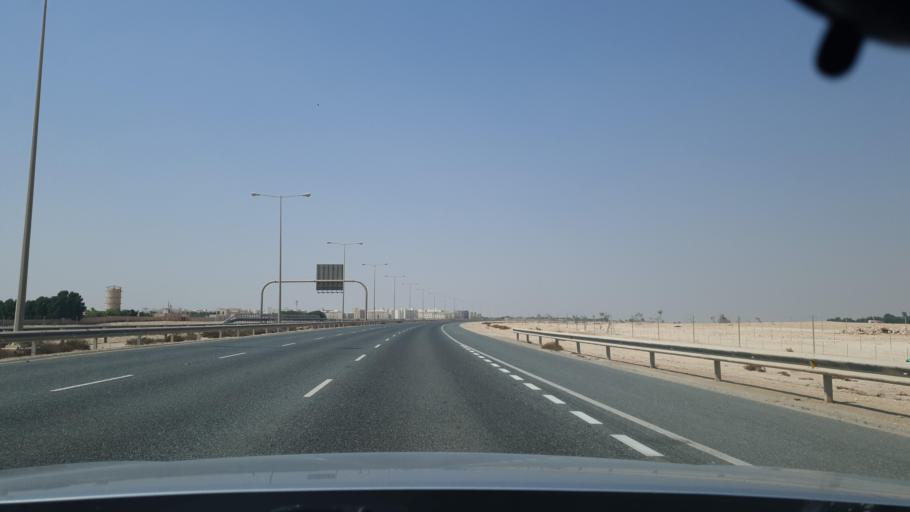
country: QA
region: Al Khawr
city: Al Khawr
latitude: 25.7554
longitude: 51.4327
